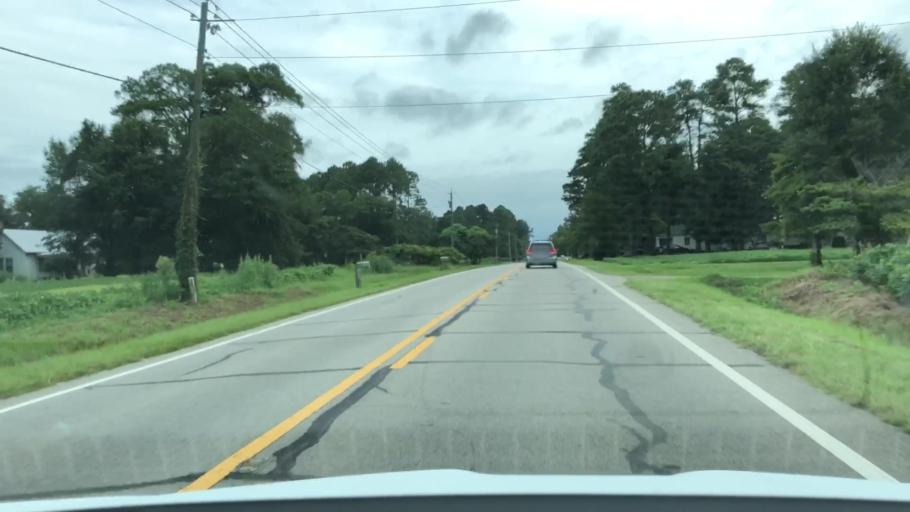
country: US
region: North Carolina
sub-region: Lenoir County
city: Kinston
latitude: 35.2106
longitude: -77.5681
